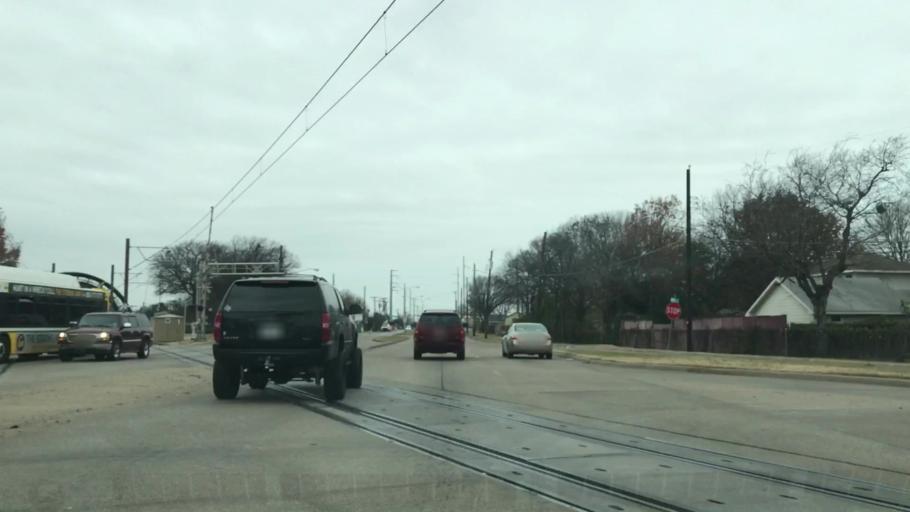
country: US
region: Texas
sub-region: Dallas County
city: Cockrell Hill
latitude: 32.7204
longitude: -96.8698
